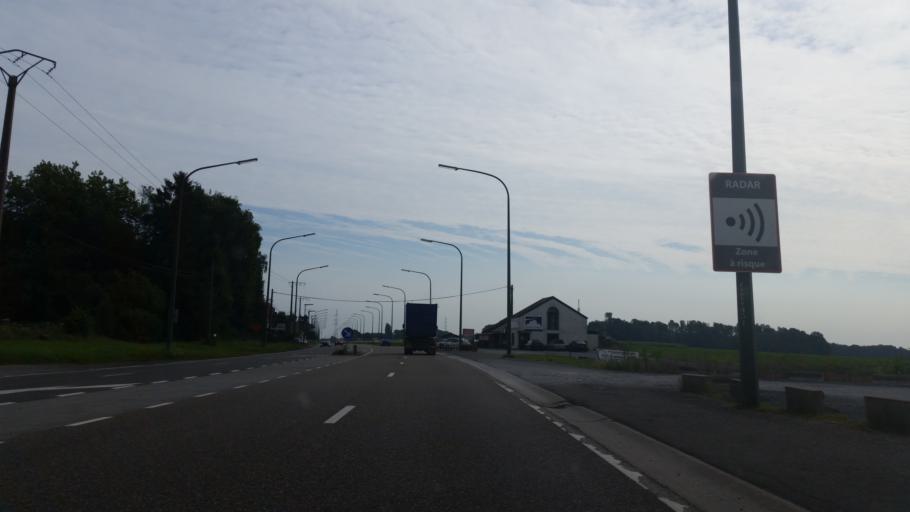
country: BE
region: Wallonia
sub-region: Province de Liege
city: Nandrin
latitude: 50.5145
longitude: 5.4065
